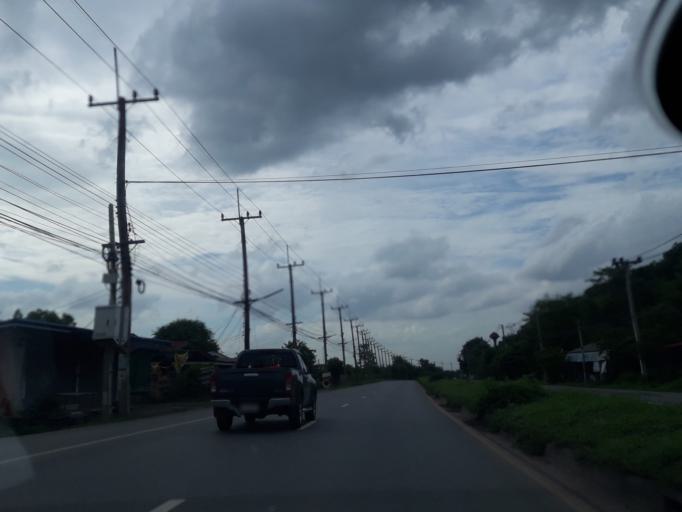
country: TH
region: Sara Buri
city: Kaeng Khoi
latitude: 14.5259
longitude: 101.0100
